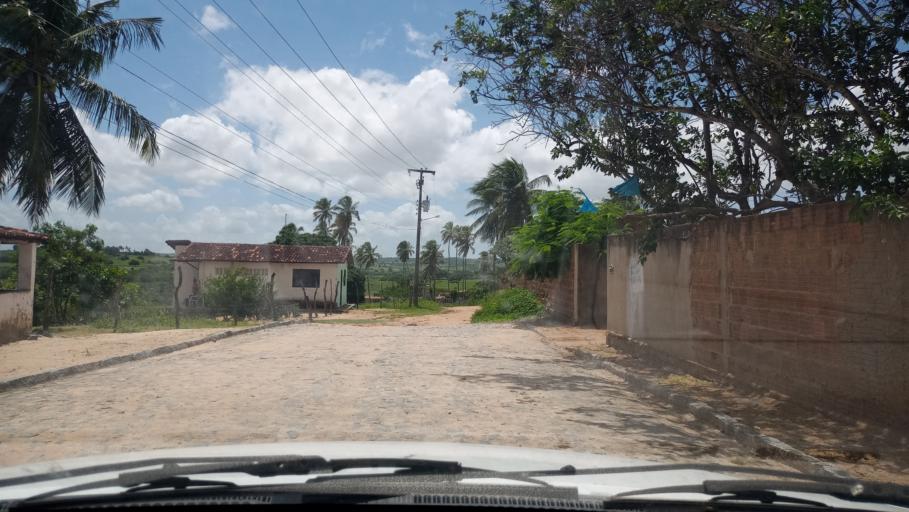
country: BR
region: Rio Grande do Norte
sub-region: Brejinho
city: Brejinho
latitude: -6.2634
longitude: -35.3747
